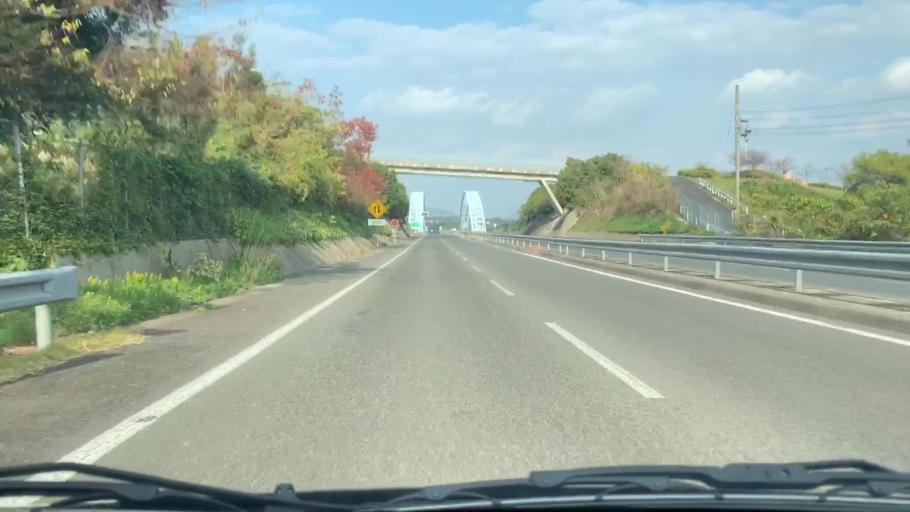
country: JP
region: Nagasaki
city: Sasebo
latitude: 33.0510
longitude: 129.7528
